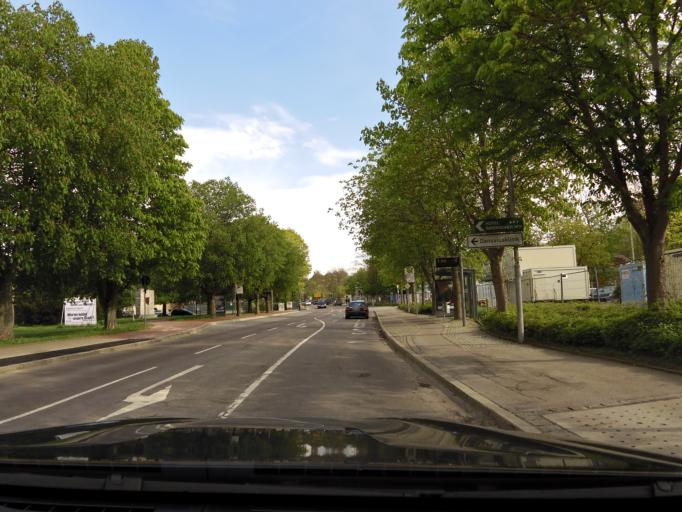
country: DE
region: Bavaria
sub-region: Upper Bavaria
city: Ingolstadt
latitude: 48.7605
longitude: 11.4220
